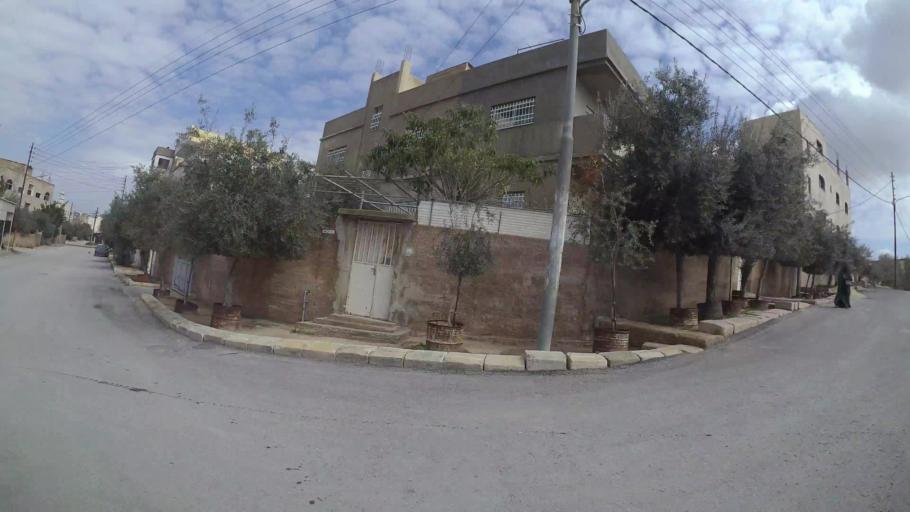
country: JO
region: Amman
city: Al Jubayhah
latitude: 32.0627
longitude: 35.8310
